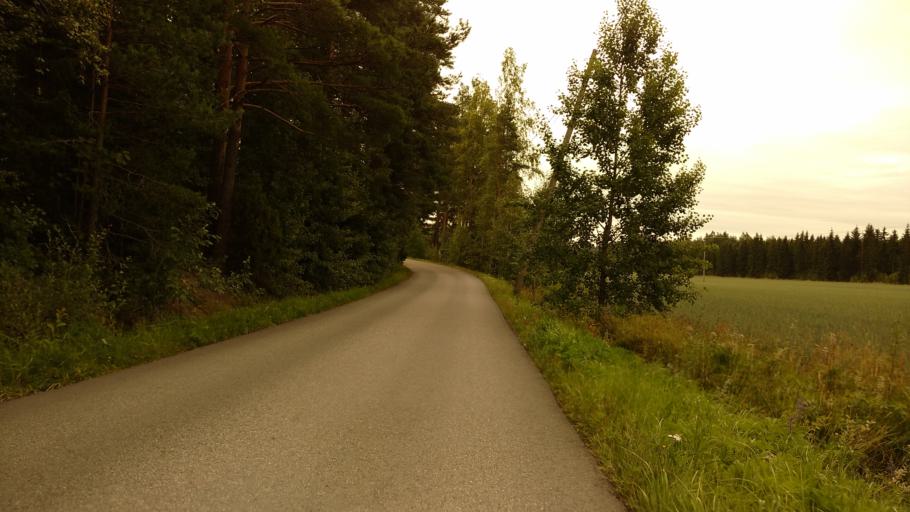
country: FI
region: Varsinais-Suomi
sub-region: Turku
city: Lieto
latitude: 60.4393
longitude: 22.4405
